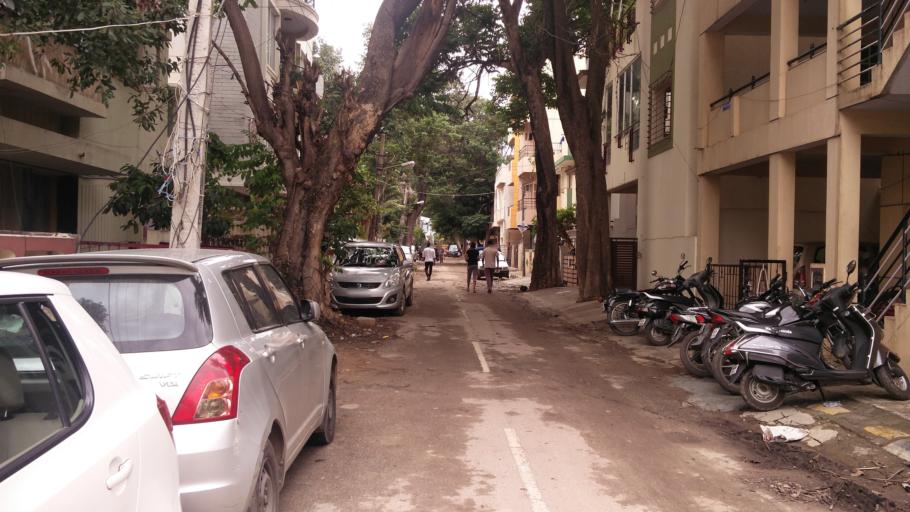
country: IN
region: Karnataka
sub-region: Bangalore Urban
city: Bangalore
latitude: 12.9777
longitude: 77.6341
